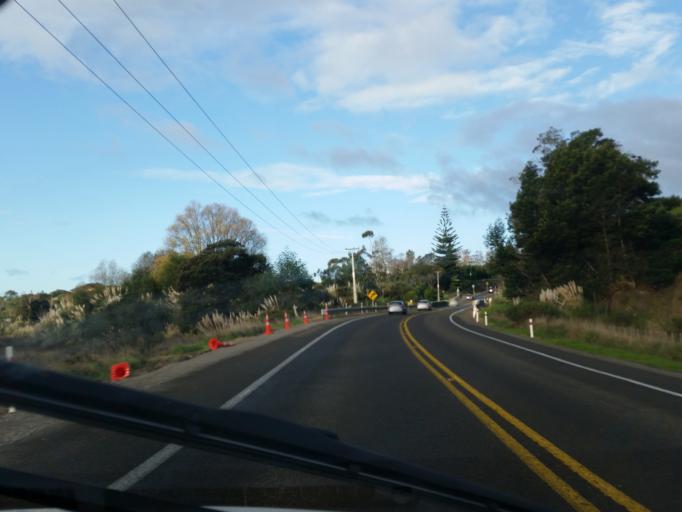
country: NZ
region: Bay of Plenty
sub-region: Tauranga City
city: Tauranga
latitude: -37.6836
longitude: 176.0337
